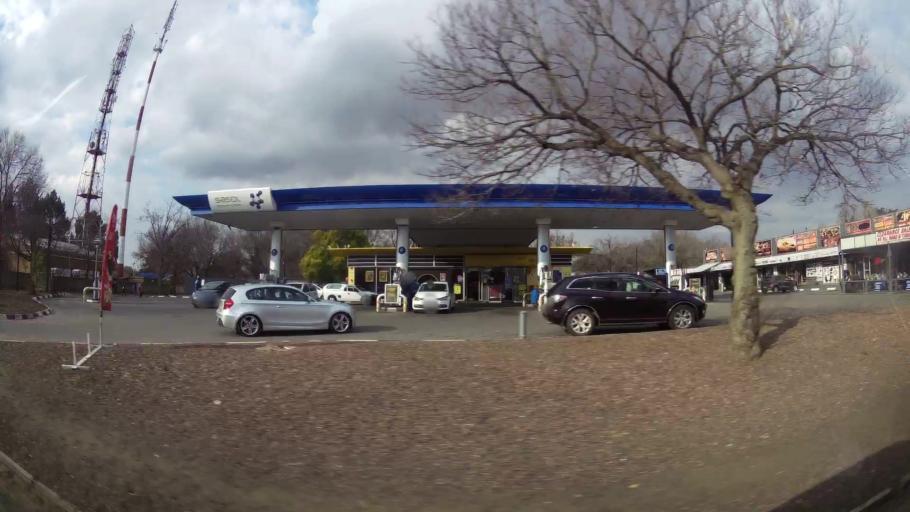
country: ZA
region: Orange Free State
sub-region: Fezile Dabi District Municipality
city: Sasolburg
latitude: -26.8172
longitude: 27.8303
